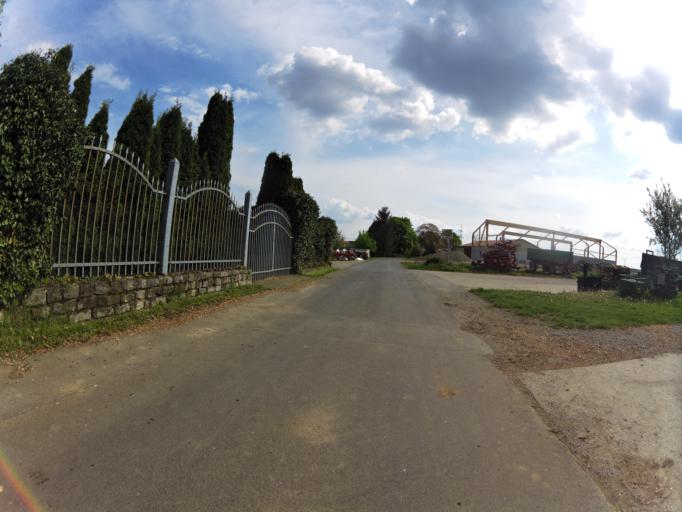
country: DE
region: Bavaria
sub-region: Regierungsbezirk Unterfranken
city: Giebelstadt
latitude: 49.6106
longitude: 9.9465
